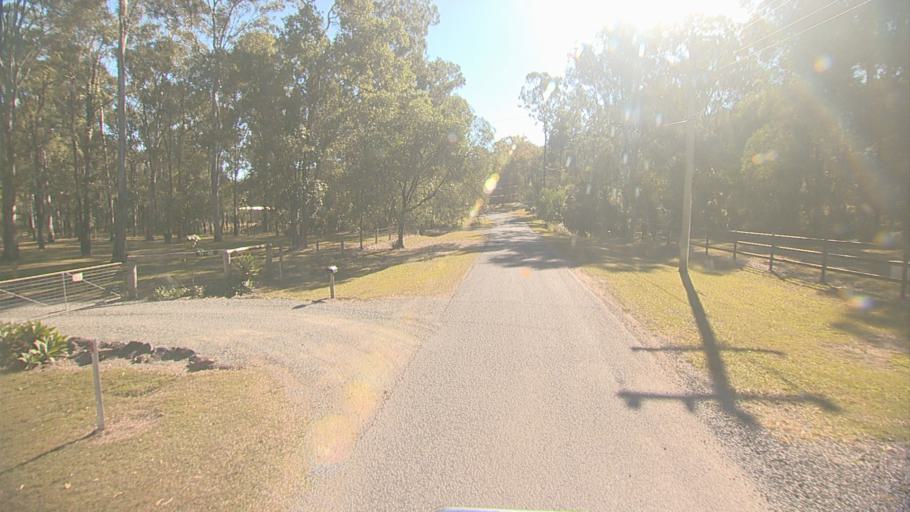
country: AU
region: Queensland
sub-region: Logan
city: Windaroo
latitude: -27.7920
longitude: 153.1469
